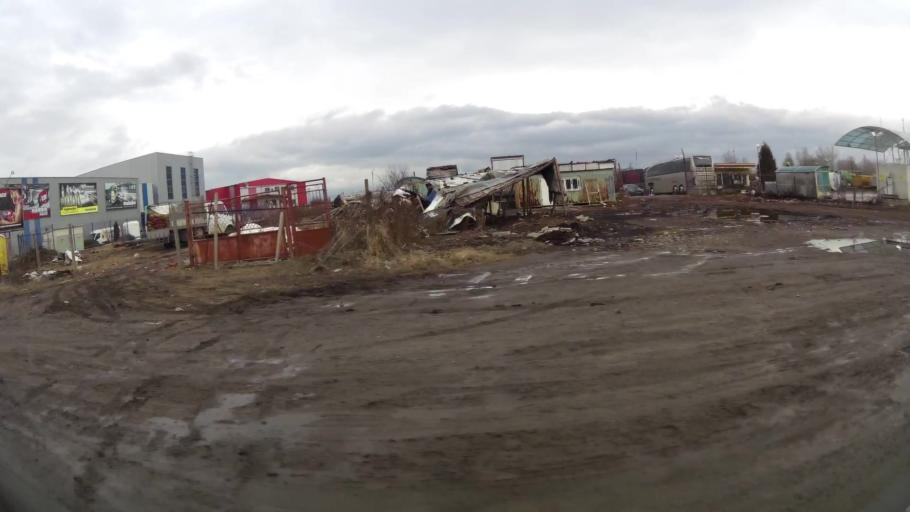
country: BG
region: Sofiya
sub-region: Obshtina Bozhurishte
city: Bozhurishte
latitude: 42.7544
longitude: 23.2725
